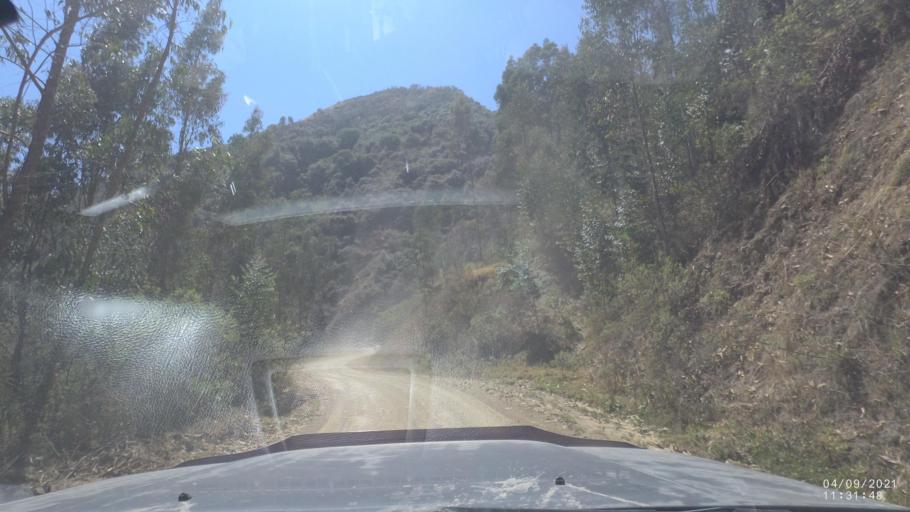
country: BO
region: Cochabamba
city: Colchani
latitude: -17.2314
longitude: -66.5209
